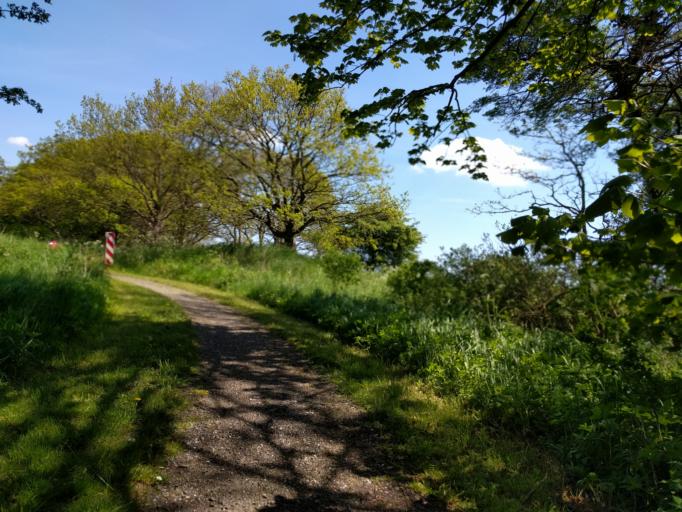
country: DK
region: Zealand
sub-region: Guldborgsund Kommune
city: Stubbekobing
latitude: 54.7592
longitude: 12.0419
